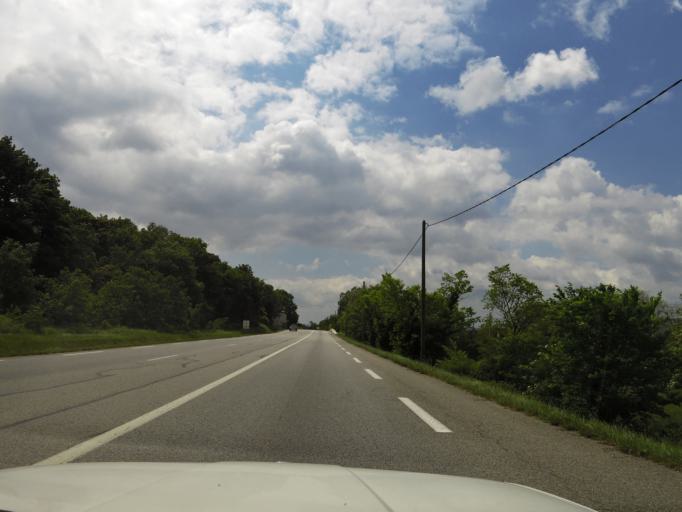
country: FR
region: Rhone-Alpes
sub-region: Departement de la Drome
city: Savasse
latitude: 44.6203
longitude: 4.7599
